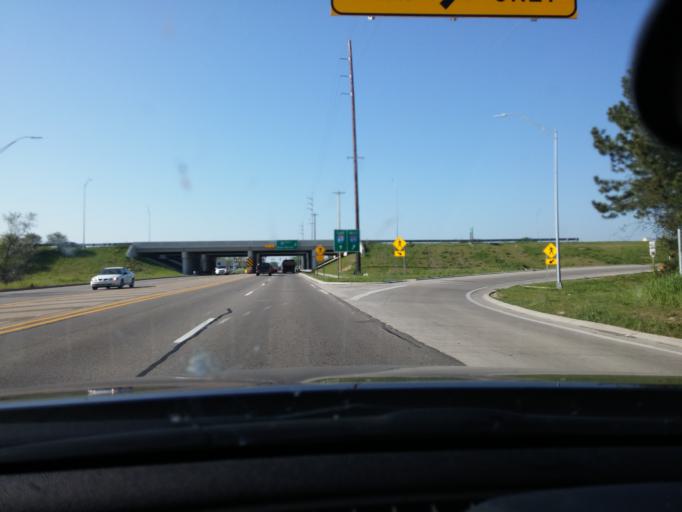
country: US
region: Michigan
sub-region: Genesee County
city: Burton
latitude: 43.0152
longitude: -83.6349
